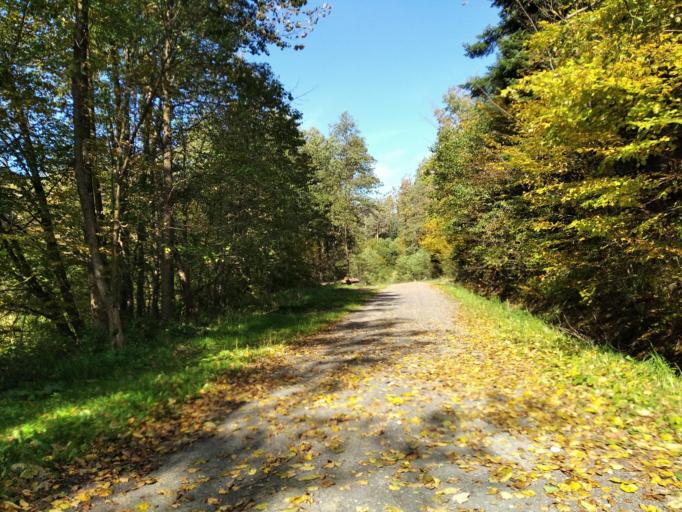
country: PL
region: Subcarpathian Voivodeship
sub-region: Powiat strzyzowski
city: Strzyzow
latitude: 49.8024
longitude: 21.8149
